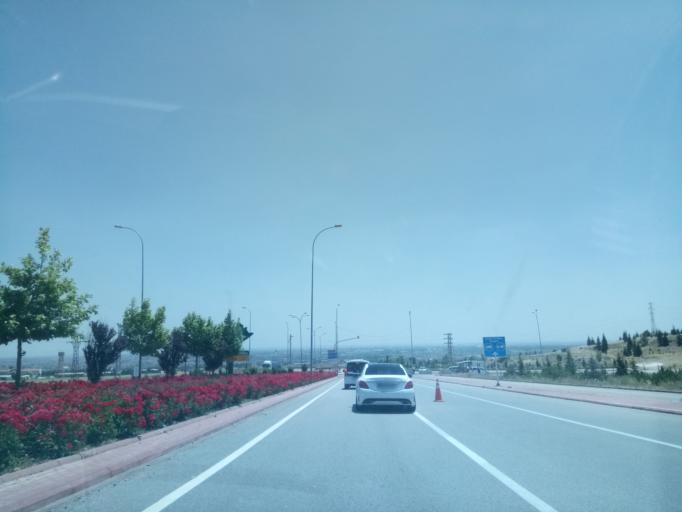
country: TR
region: Konya
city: Hatip
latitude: 37.8137
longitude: 32.3909
